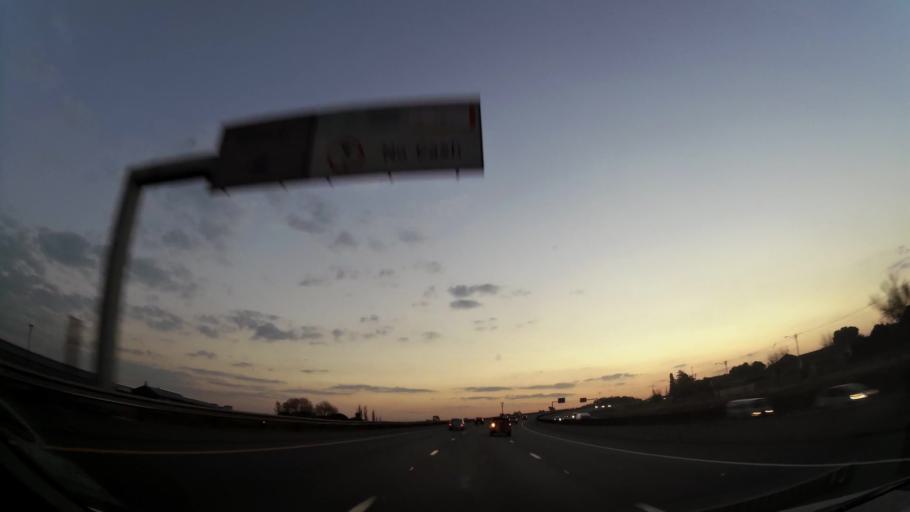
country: ZA
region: Gauteng
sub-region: Ekurhuleni Metropolitan Municipality
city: Germiston
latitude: -26.2579
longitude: 28.1781
